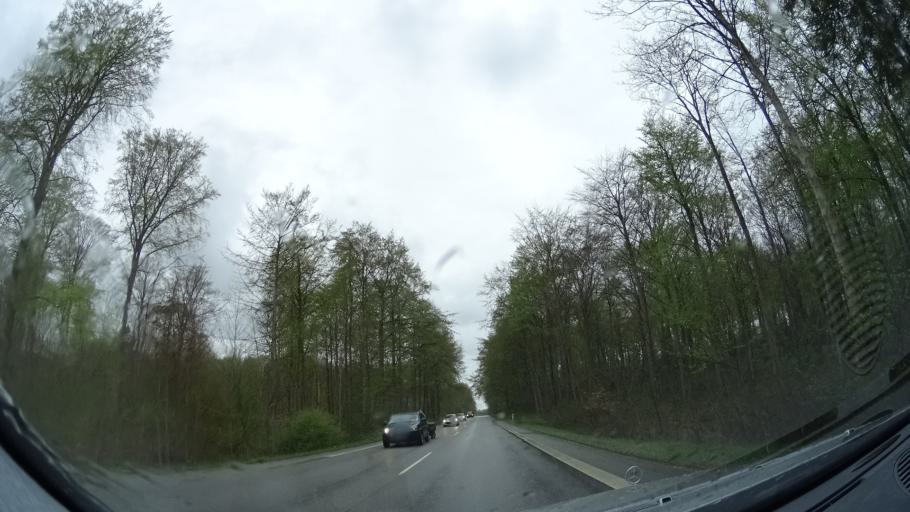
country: DK
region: Zealand
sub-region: Lejre Kommune
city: Ejby
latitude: 55.6840
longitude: 11.7997
